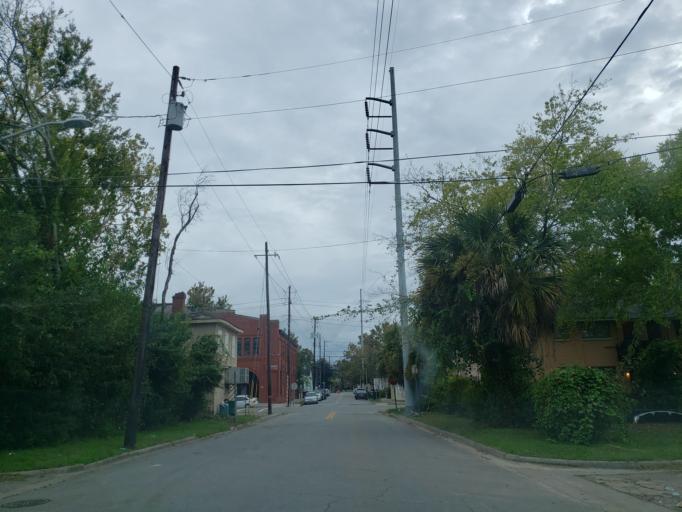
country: US
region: Georgia
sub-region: Chatham County
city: Savannah
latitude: 32.0645
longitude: -81.0835
